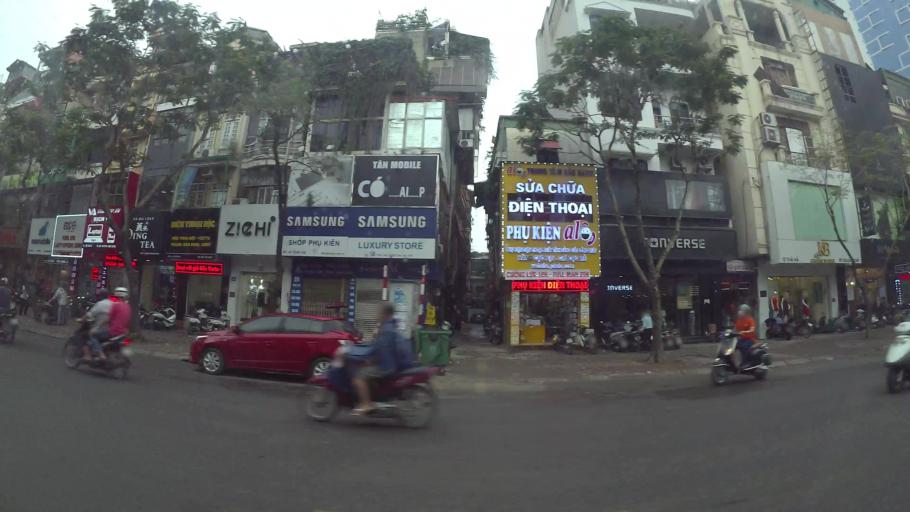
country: VN
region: Ha Noi
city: Dong Da
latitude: 21.0102
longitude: 105.8230
